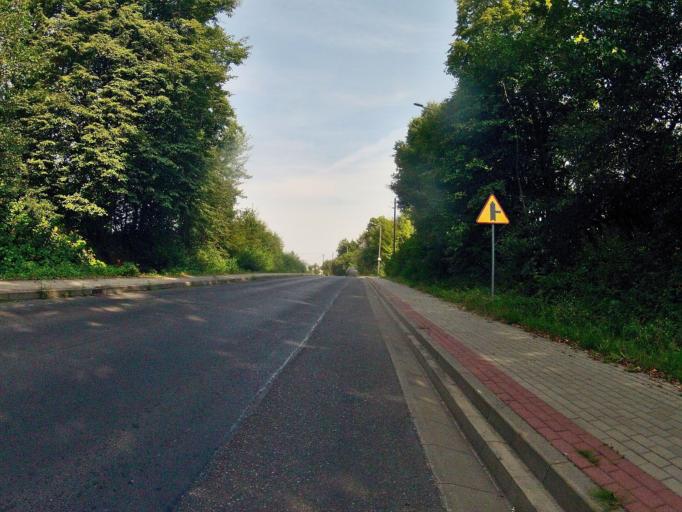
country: PL
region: Subcarpathian Voivodeship
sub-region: Powiat jasielski
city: Trzcinica
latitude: 49.7560
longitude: 21.4442
